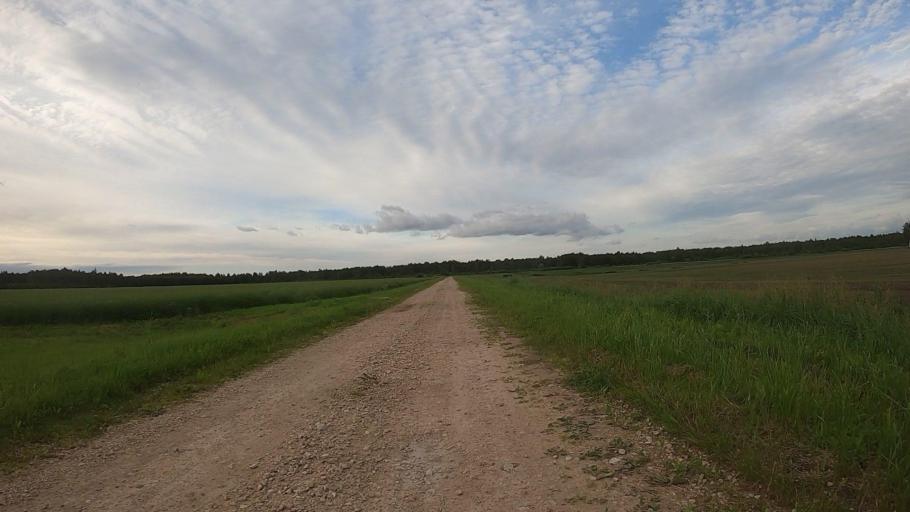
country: LV
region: Olaine
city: Olaine
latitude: 56.8249
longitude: 23.9569
